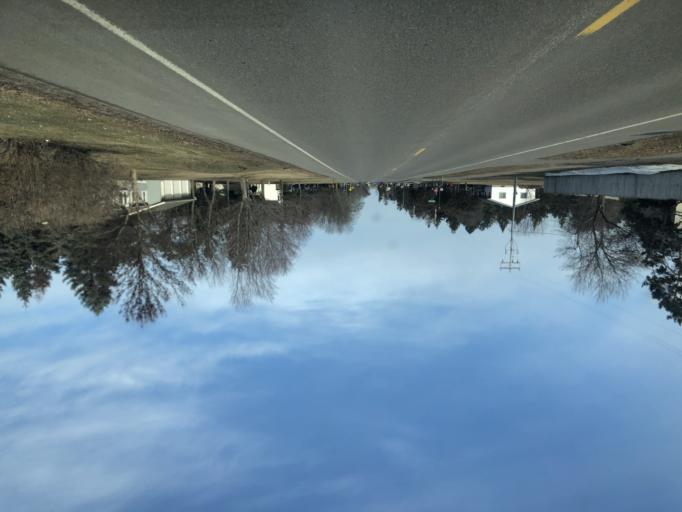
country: US
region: Minnesota
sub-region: Sherburne County
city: Becker
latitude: 45.3937
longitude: -93.8638
